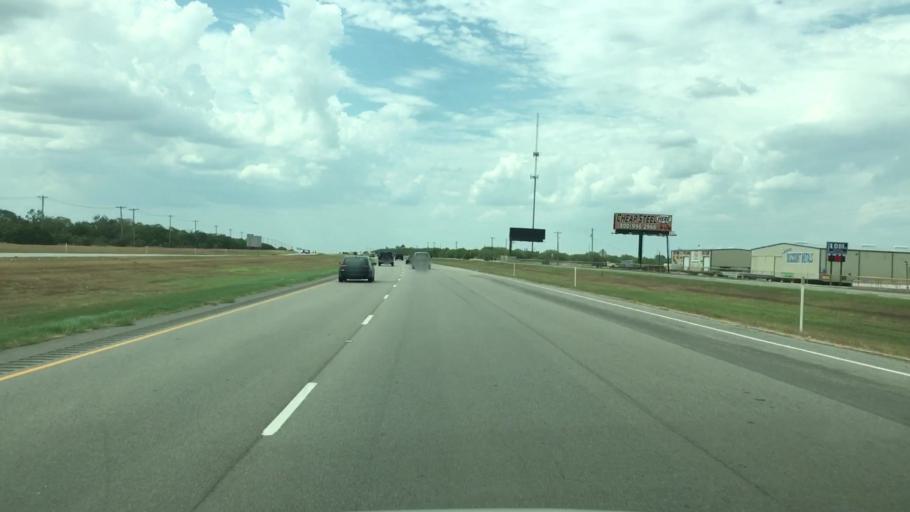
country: US
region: Texas
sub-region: Live Oak County
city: Three Rivers
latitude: 28.4931
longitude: -98.1469
